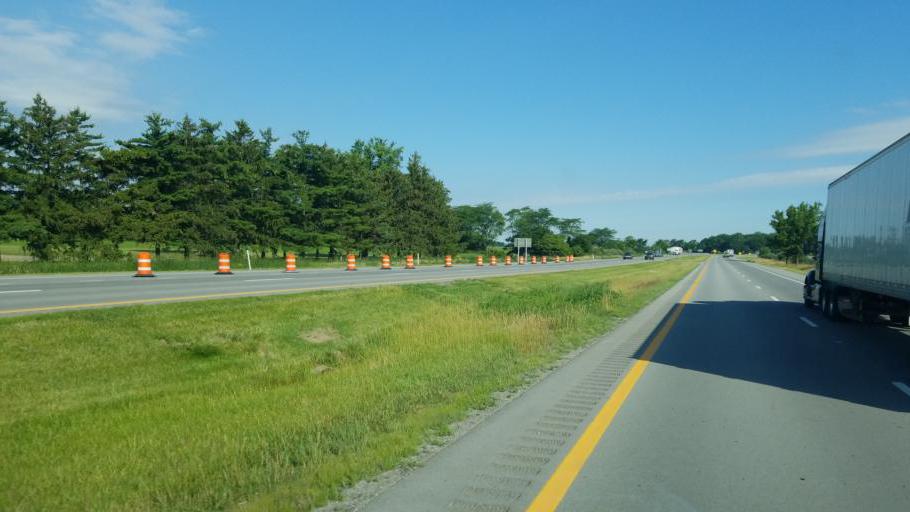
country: US
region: Ohio
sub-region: Hancock County
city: Findlay
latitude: 40.9973
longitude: -83.6543
